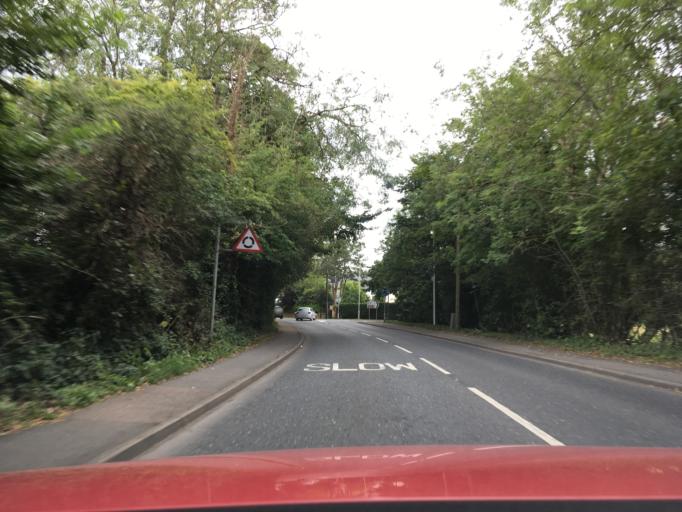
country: GB
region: England
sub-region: West Berkshire
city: Newbury
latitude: 51.4134
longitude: -1.3322
